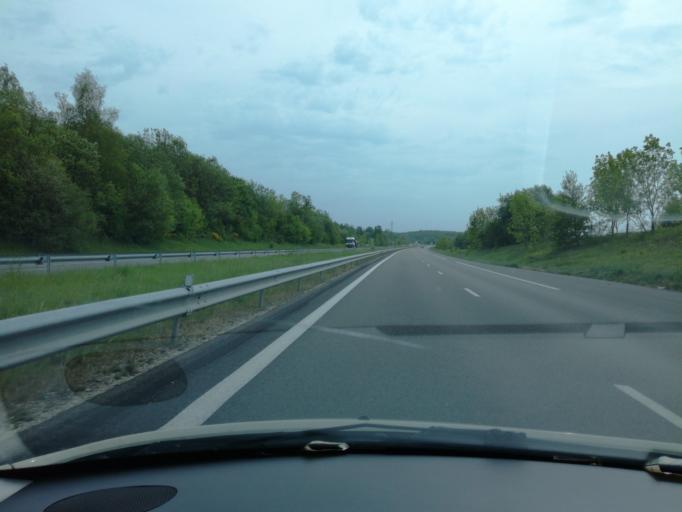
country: FR
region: Rhone-Alpes
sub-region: Departement de l'Ain
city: Marboz
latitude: 46.3329
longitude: 5.2775
